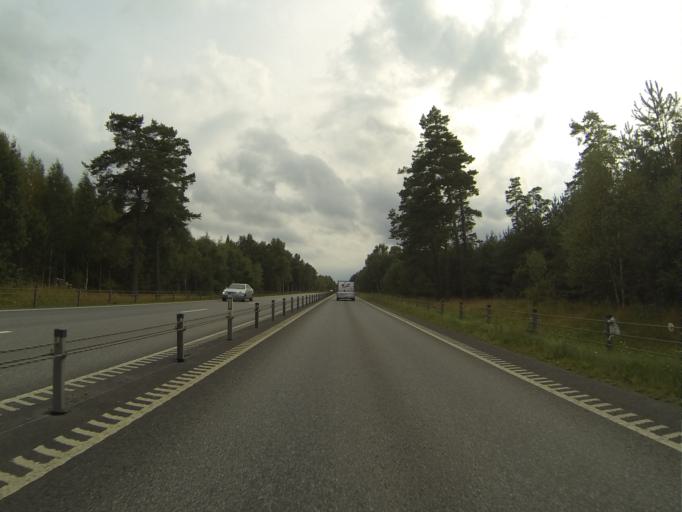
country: SE
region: Skane
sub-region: Kristianstads Kommun
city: Norra Asum
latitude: 55.9757
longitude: 14.0820
